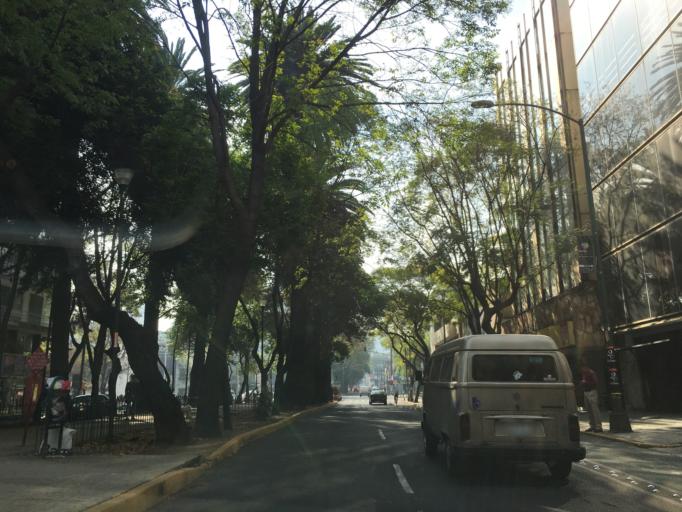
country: MX
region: Mexico City
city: Benito Juarez
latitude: 19.4085
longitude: -99.1724
